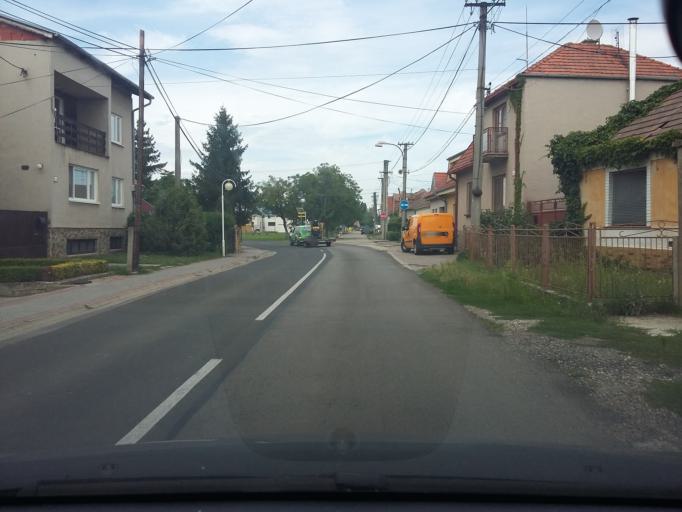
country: SK
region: Bratislavsky
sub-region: Okres Pezinok
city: Pezinok
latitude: 48.2528
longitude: 17.2846
